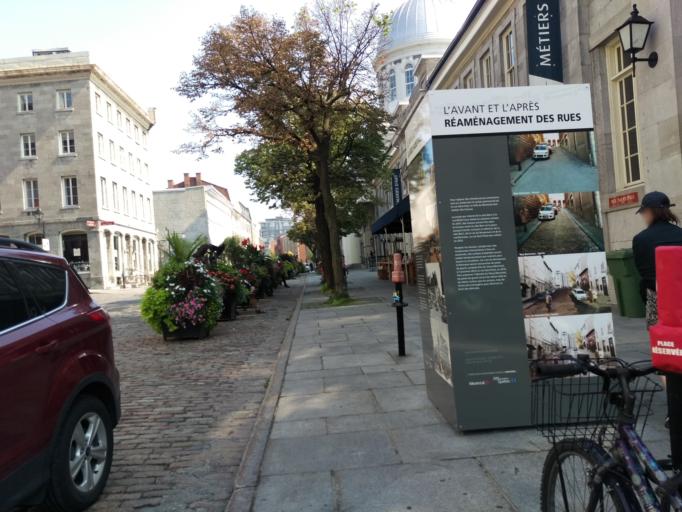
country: CA
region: Quebec
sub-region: Montreal
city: Montreal
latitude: 45.5083
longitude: -73.5521
